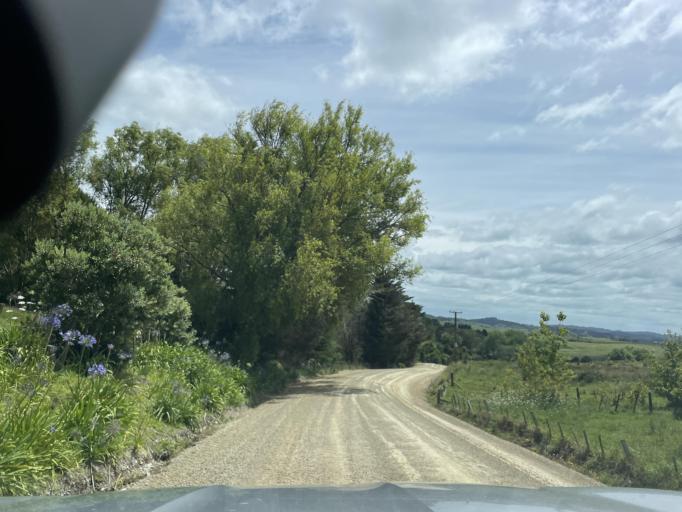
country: NZ
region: Auckland
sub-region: Auckland
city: Wellsford
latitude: -36.1490
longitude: 174.2818
